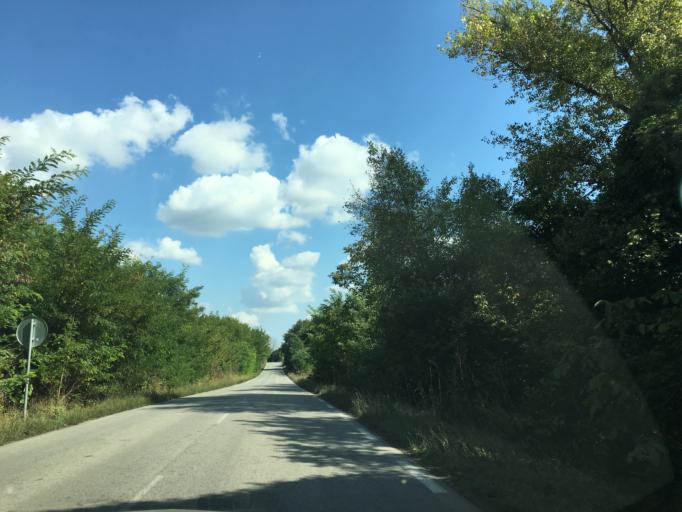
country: BG
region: Montana
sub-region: Obshtina Lom
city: Lom
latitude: 43.8126
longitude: 23.1801
